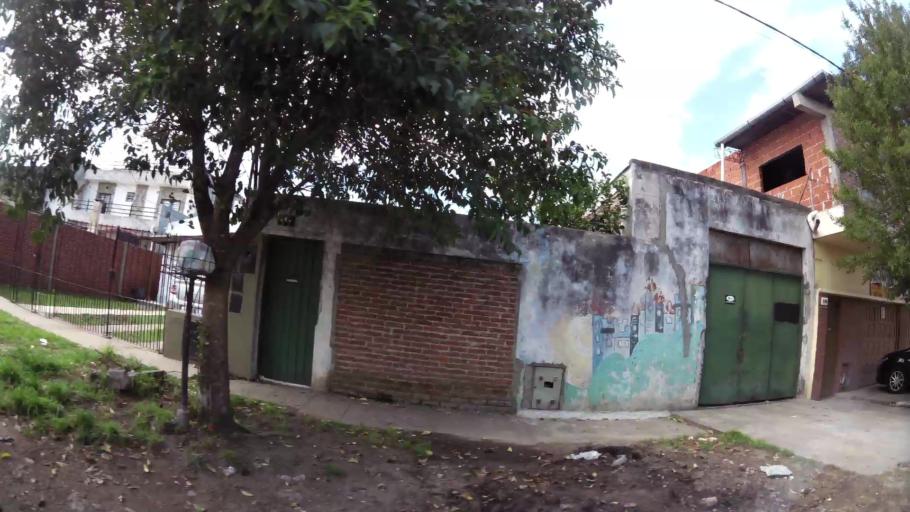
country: AR
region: Buenos Aires
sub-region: Partido de Quilmes
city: Quilmes
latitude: -34.7789
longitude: -58.2755
